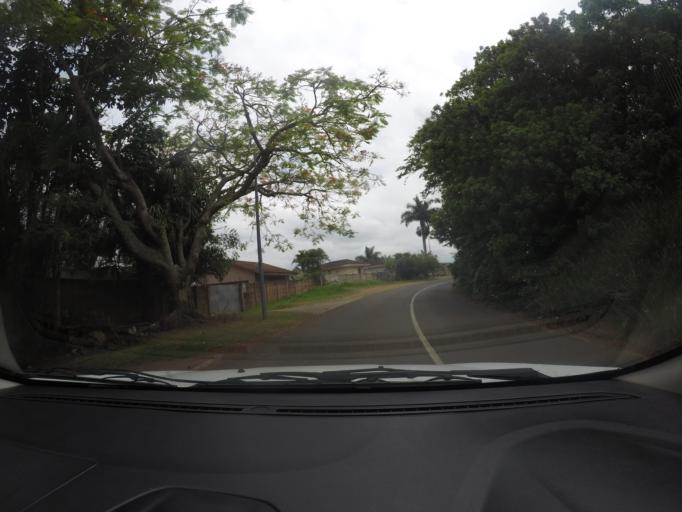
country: ZA
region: KwaZulu-Natal
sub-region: uThungulu District Municipality
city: Empangeni
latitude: -28.7517
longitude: 31.8910
